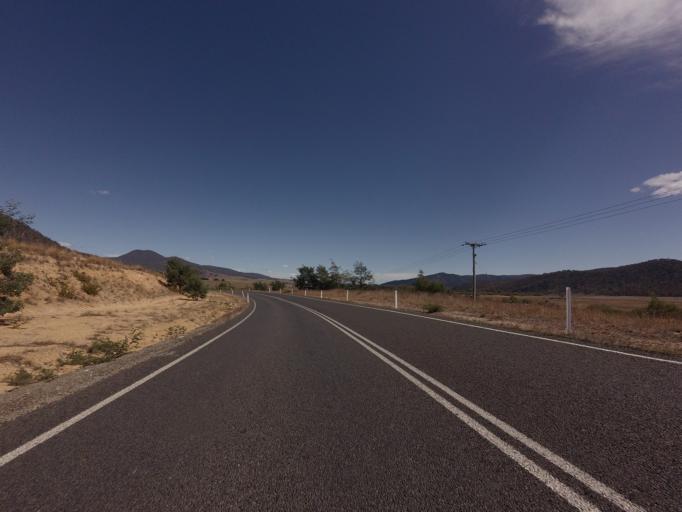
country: AU
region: Tasmania
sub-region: Break O'Day
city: St Helens
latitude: -41.6957
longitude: 147.8629
